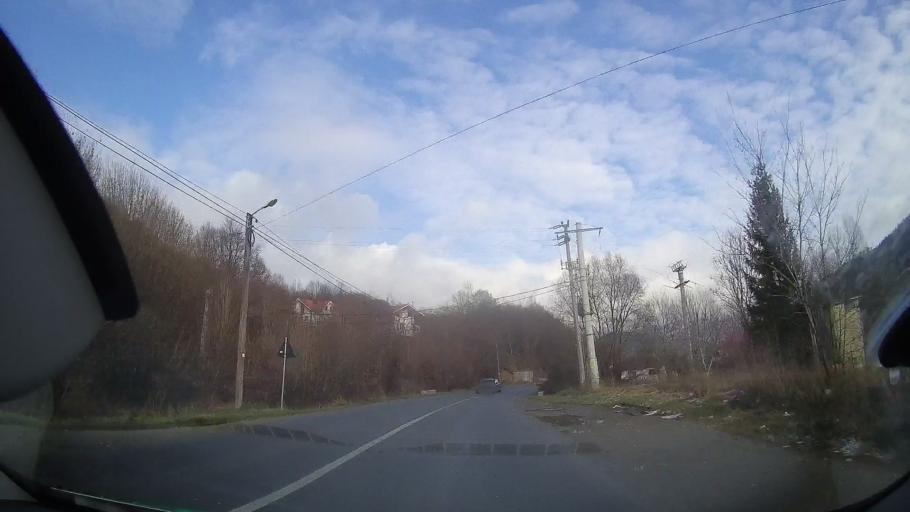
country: RO
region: Alba
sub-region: Comuna Bistra
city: Bistra
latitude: 46.3633
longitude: 23.0806
